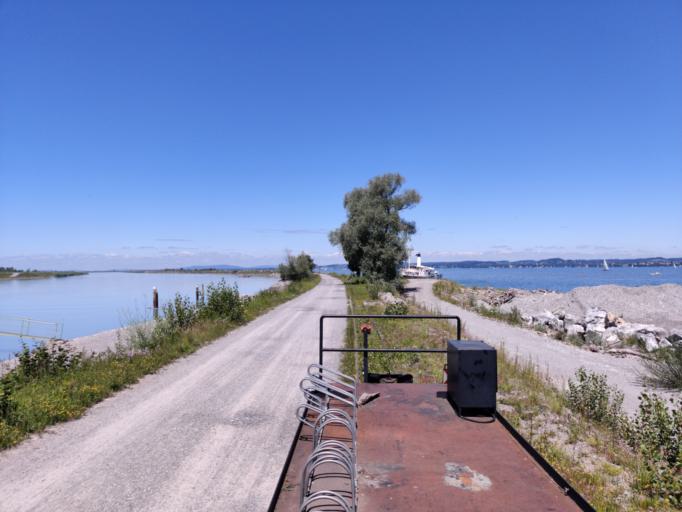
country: AT
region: Vorarlberg
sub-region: Politischer Bezirk Bregenz
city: Hard
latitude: 47.5045
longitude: 9.6706
